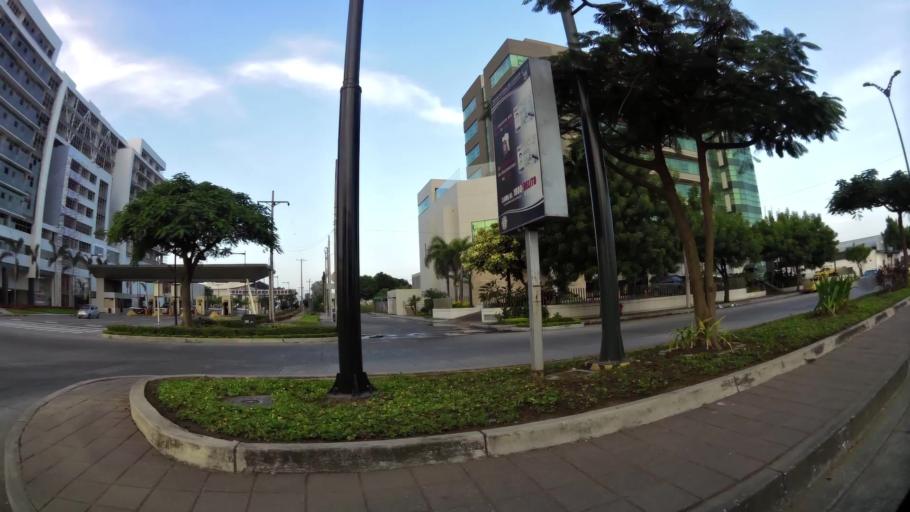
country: EC
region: Guayas
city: Eloy Alfaro
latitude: -2.1450
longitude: -79.8831
